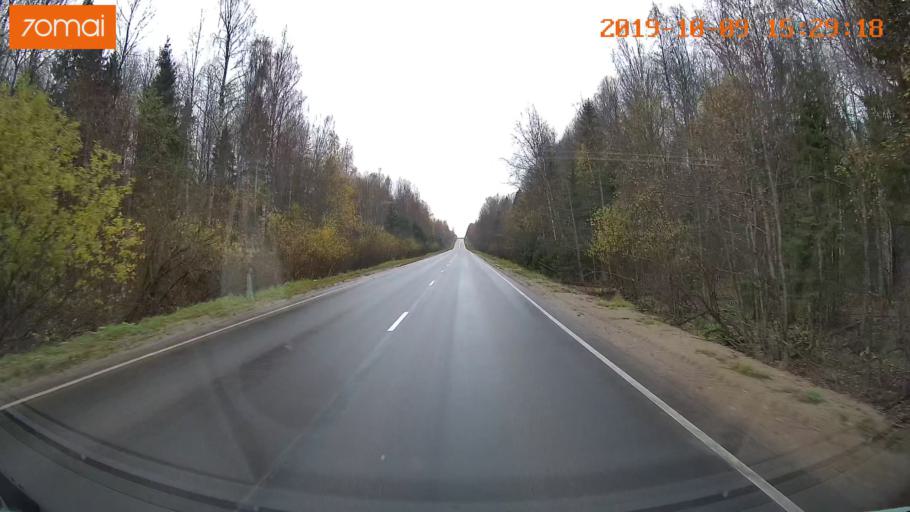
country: RU
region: Kostroma
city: Susanino
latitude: 57.9930
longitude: 41.3451
